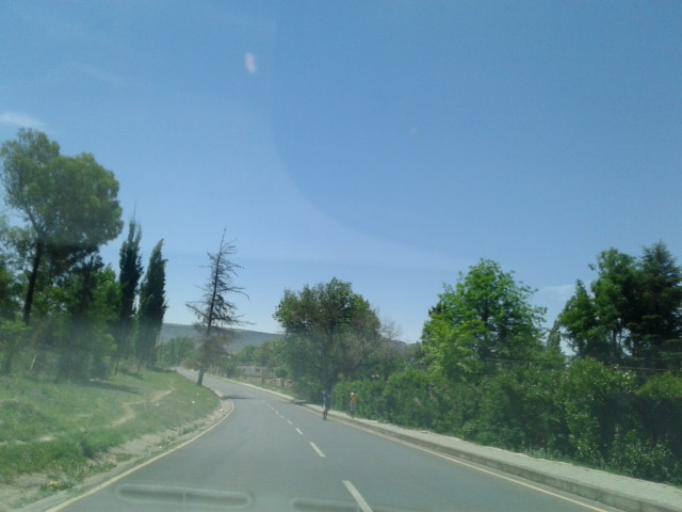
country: LS
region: Maseru
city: Maseru
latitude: -29.3068
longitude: 27.4792
